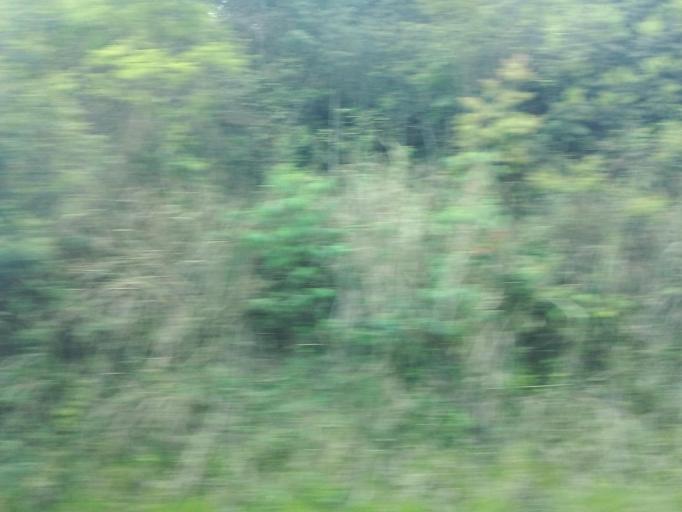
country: BR
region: Minas Gerais
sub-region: Rio Piracicaba
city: Rio Piracicaba
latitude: -19.9730
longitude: -43.2106
